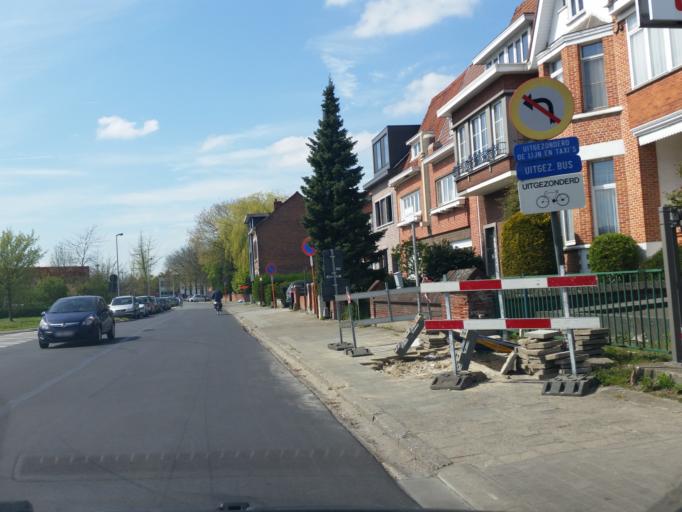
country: BE
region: Flanders
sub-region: Provincie Oost-Vlaanderen
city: Sint-Niklaas
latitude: 51.1741
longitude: 4.1506
